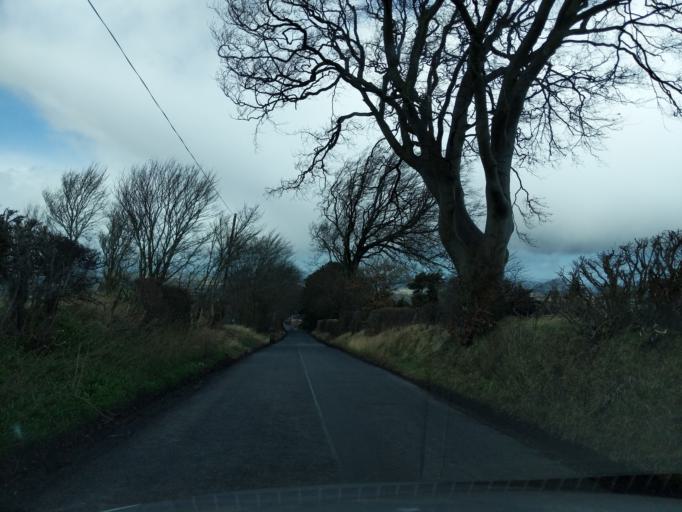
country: GB
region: Scotland
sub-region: Edinburgh
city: Currie
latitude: 55.8900
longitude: -3.3037
